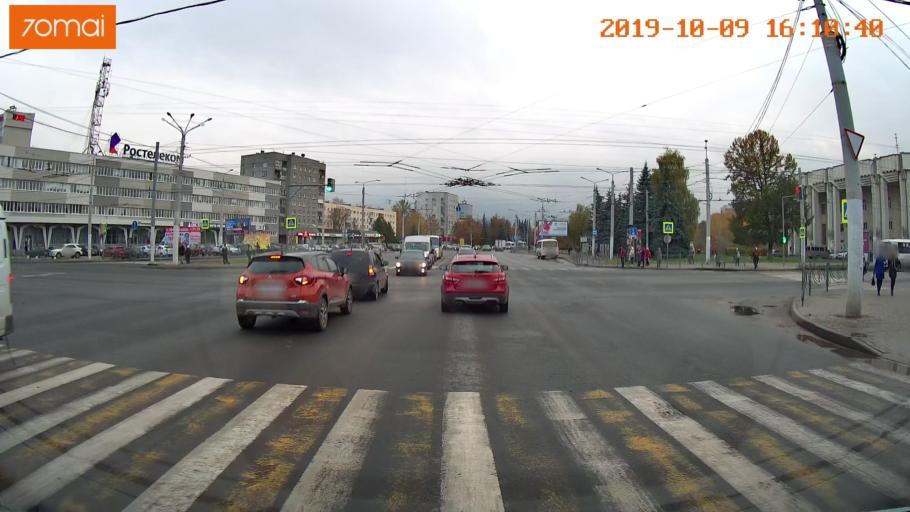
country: RU
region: Kostroma
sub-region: Kostromskoy Rayon
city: Kostroma
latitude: 57.7616
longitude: 40.9513
